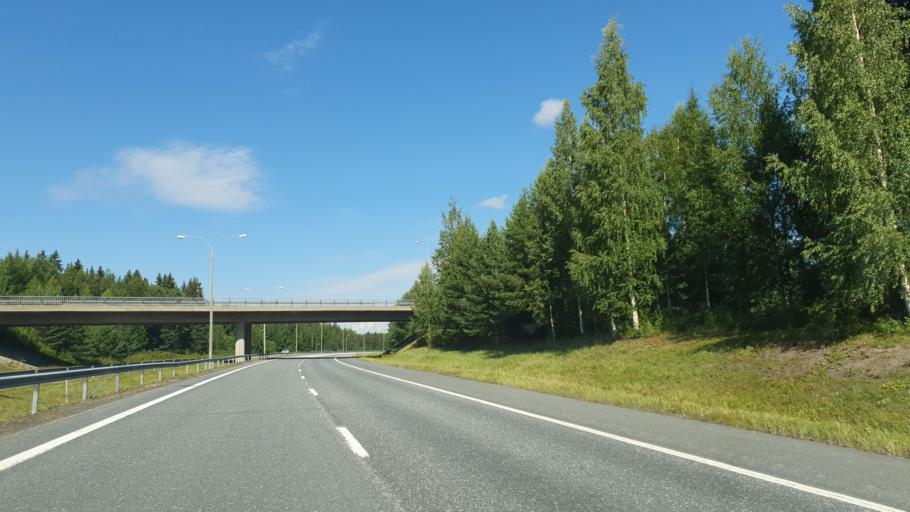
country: FI
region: Northern Savo
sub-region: Ylae-Savo
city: Iisalmi
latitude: 63.5241
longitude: 27.2492
